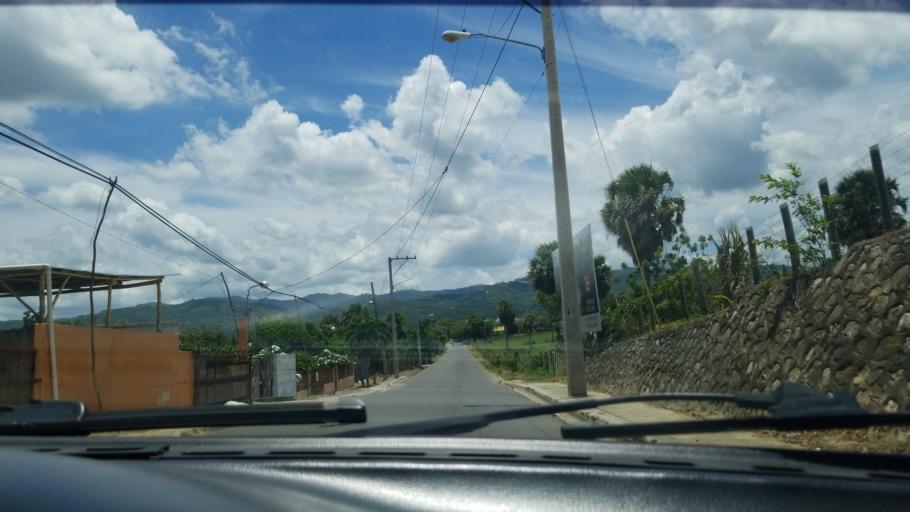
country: DO
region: Santiago
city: Santiago de los Caballeros
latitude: 19.4873
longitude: -70.6783
